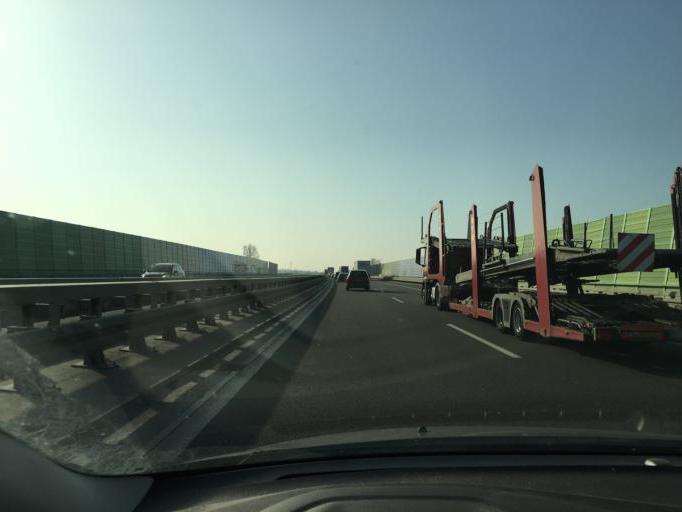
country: DE
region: Saxony
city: Borna
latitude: 51.0972
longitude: 12.5256
